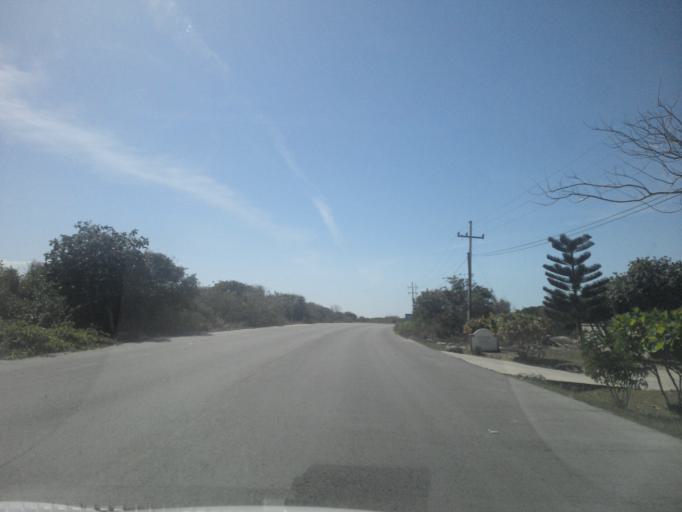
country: MX
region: Yucatan
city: Telchac Puerto
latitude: 21.3292
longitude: -89.3840
